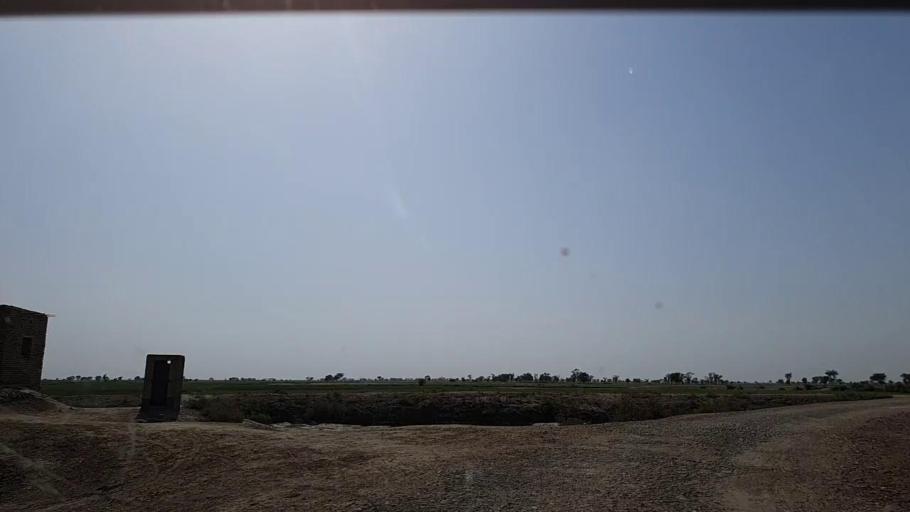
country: PK
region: Sindh
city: Phulji
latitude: 26.9208
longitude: 67.6724
